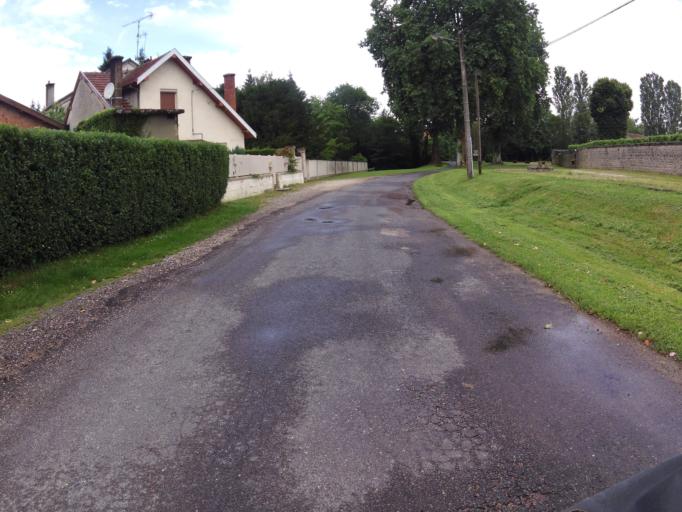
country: FR
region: Champagne-Ardenne
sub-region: Departement de la Marne
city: Sermaize-les-Bains
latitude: 48.7867
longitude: 4.9103
